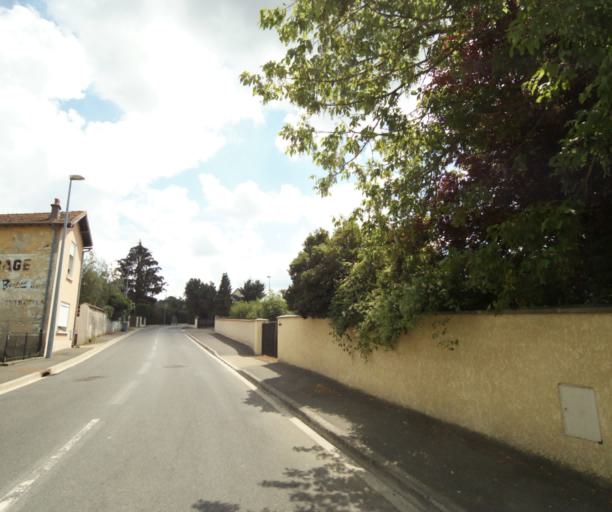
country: FR
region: Ile-de-France
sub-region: Departement de Seine-et-Marne
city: Samoreau
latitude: 48.4290
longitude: 2.7555
